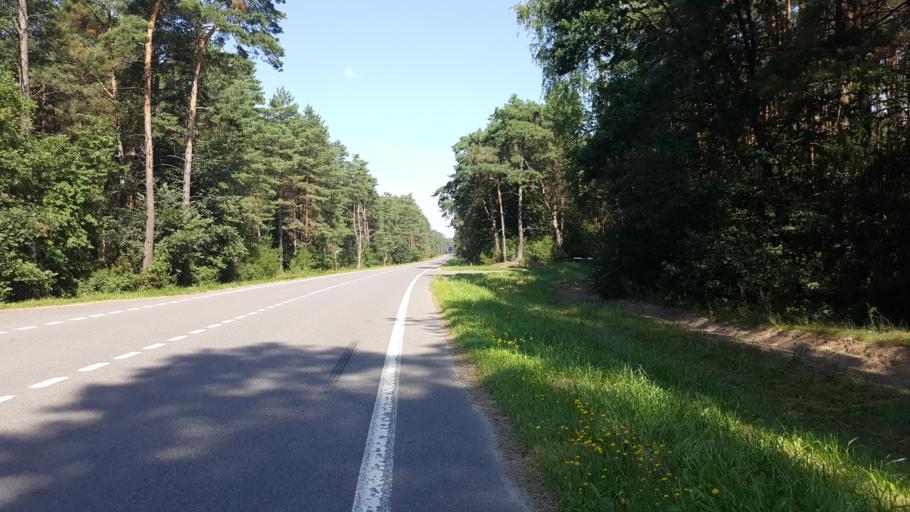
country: BY
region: Brest
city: Kamyanyuki
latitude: 52.5071
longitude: 23.6599
